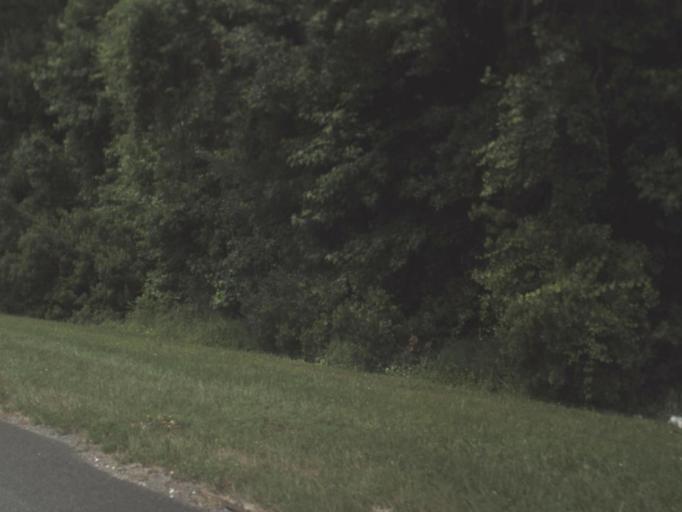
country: US
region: Florida
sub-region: Clay County
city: Green Cove Springs
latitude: 30.0528
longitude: -81.7083
